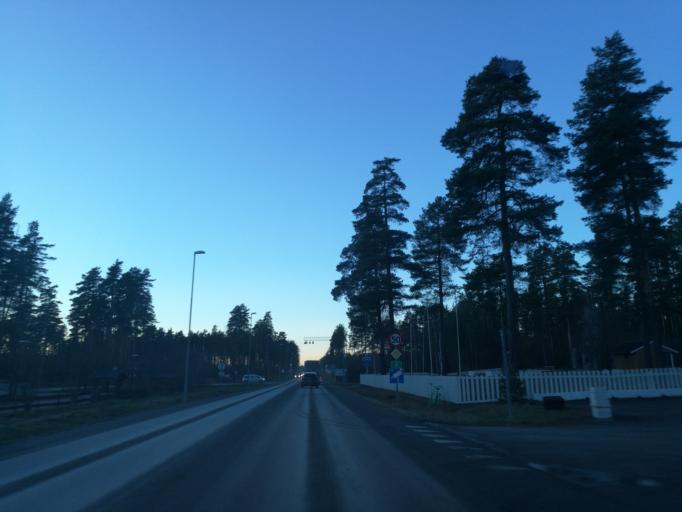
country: SE
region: Vaermland
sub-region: Eda Kommun
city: Charlottenberg
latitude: 59.9312
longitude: 12.2396
